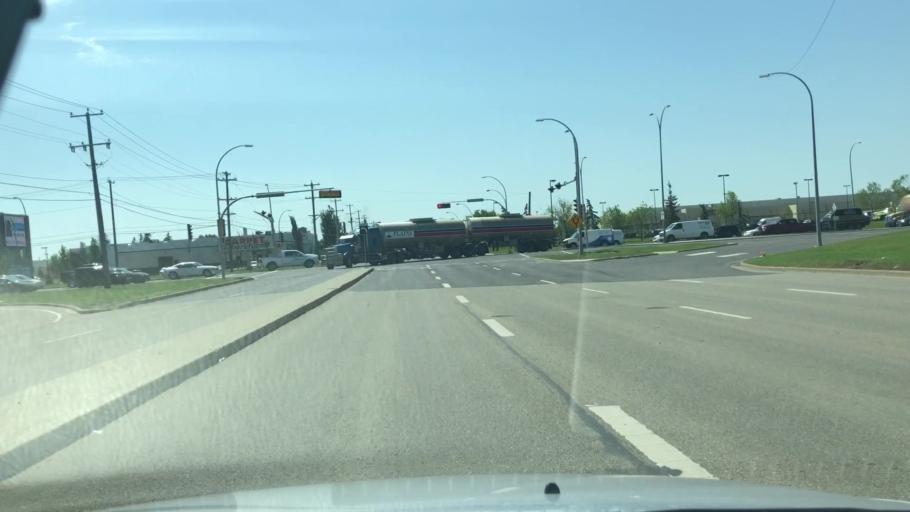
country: CA
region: Alberta
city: St. Albert
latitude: 53.5822
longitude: -113.5781
